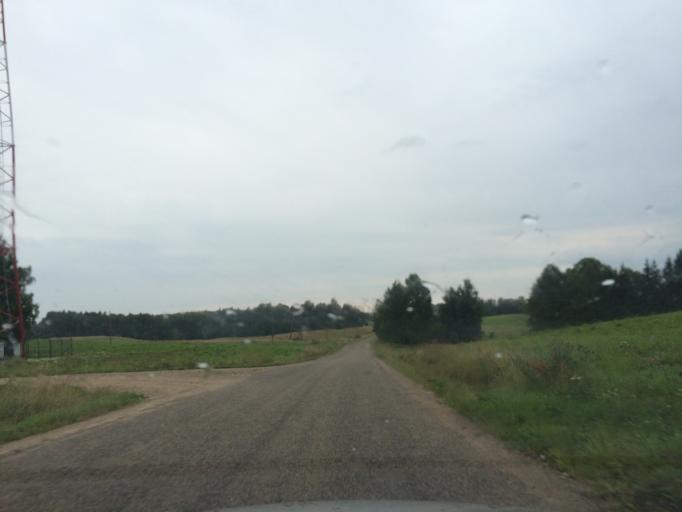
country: LV
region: Rezekne
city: Rezekne
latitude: 56.5786
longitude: 27.4934
